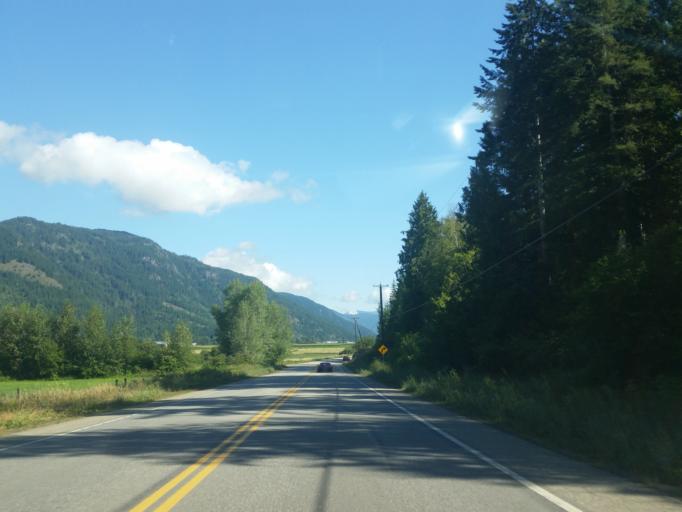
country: CA
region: British Columbia
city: Enderby
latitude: 50.6598
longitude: -119.0748
